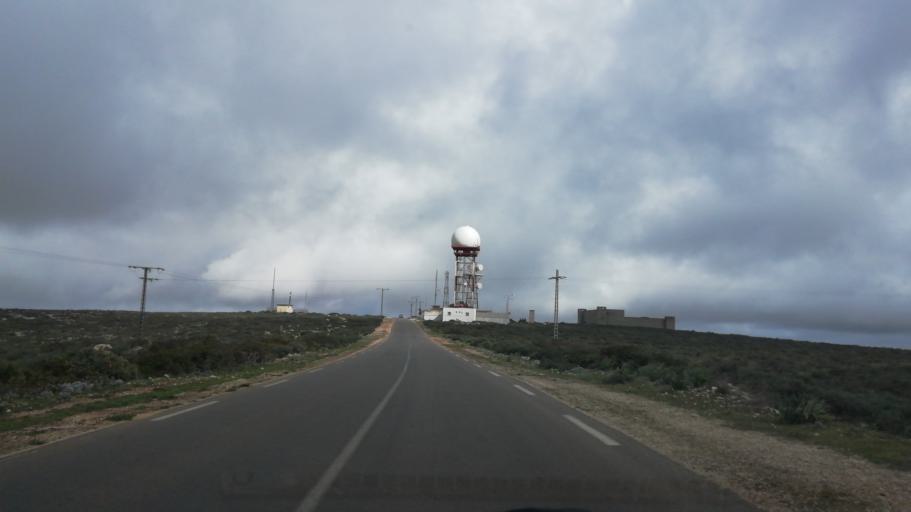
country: DZ
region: Oran
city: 'Ain el Turk
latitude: 35.6945
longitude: -0.7731
